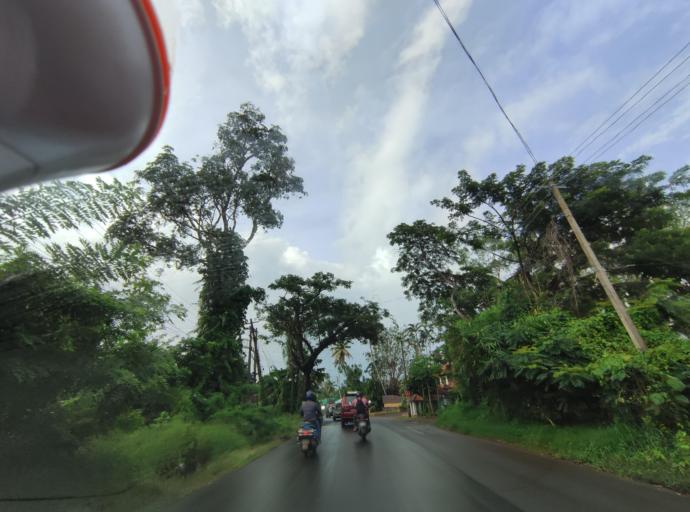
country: IN
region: Kerala
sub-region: Alappuzha
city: Shertallai
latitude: 9.6269
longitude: 76.4292
